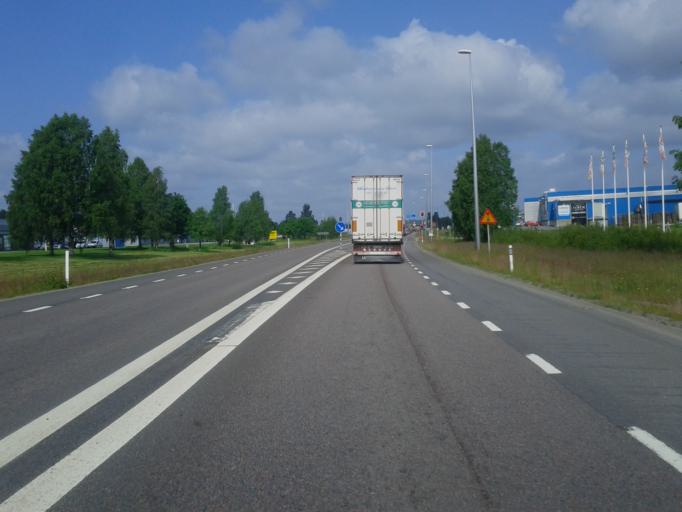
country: SE
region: Vaesterbotten
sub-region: Skelleftea Kommun
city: Skelleftea
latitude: 64.7344
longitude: 20.9692
